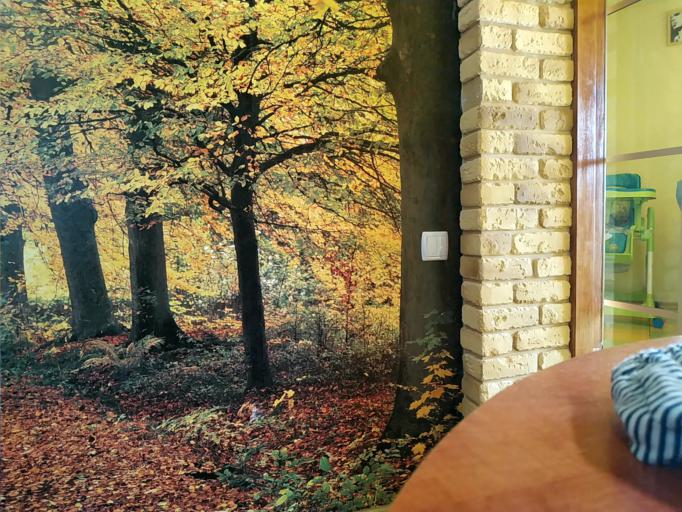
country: RU
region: Novgorod
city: Parfino
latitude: 57.7957
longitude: 31.6309
